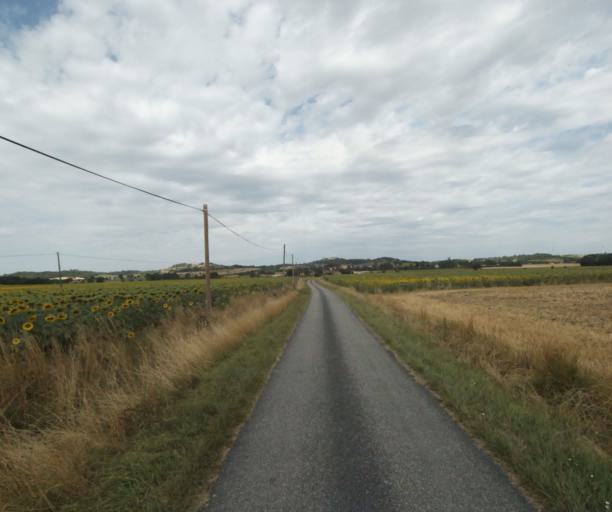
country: FR
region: Midi-Pyrenees
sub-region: Departement de la Haute-Garonne
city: Saint-Felix-Lauragais
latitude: 43.4355
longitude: 1.9201
